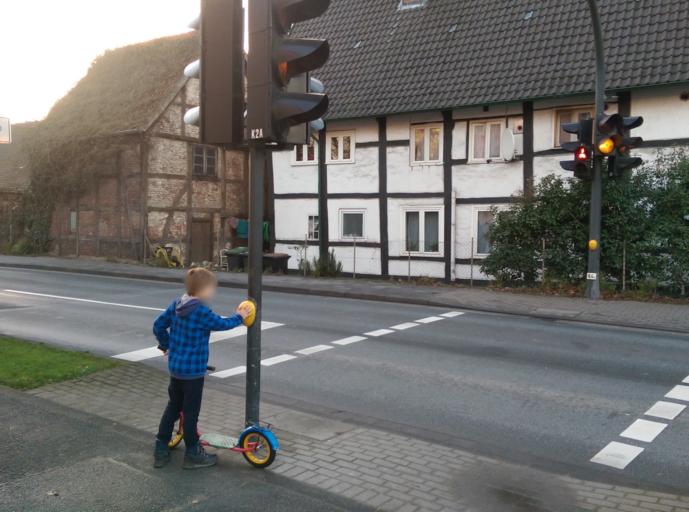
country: DE
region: North Rhine-Westphalia
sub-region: Regierungsbezirk Detmold
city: Rheda-Wiedenbruck
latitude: 51.8518
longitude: 8.2925
